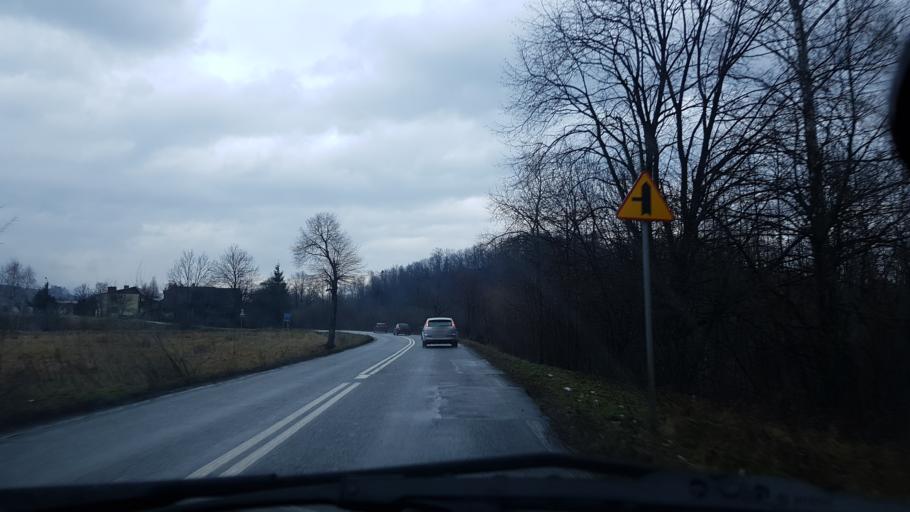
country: PL
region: Silesian Voivodeship
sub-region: Powiat zywiecki
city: Lekawica
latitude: 49.7115
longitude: 19.2580
